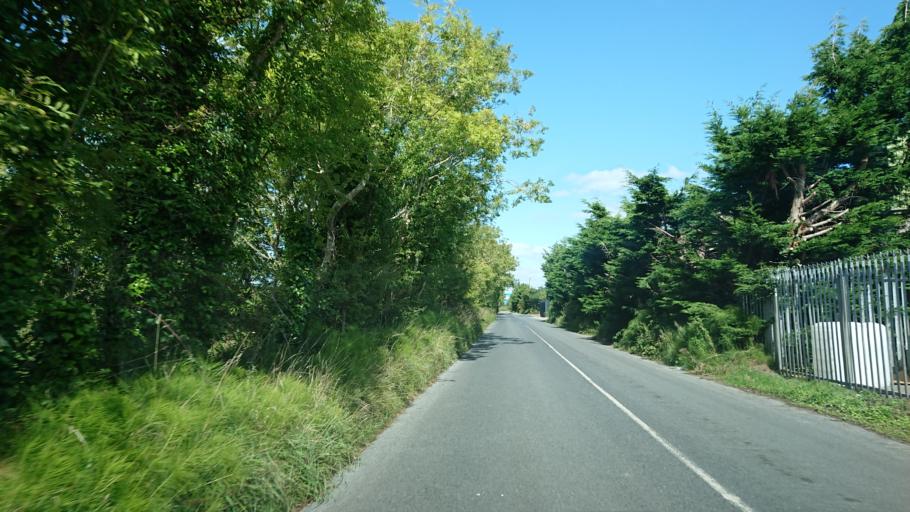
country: IE
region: Munster
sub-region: Waterford
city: Waterford
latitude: 52.2295
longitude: -7.1461
